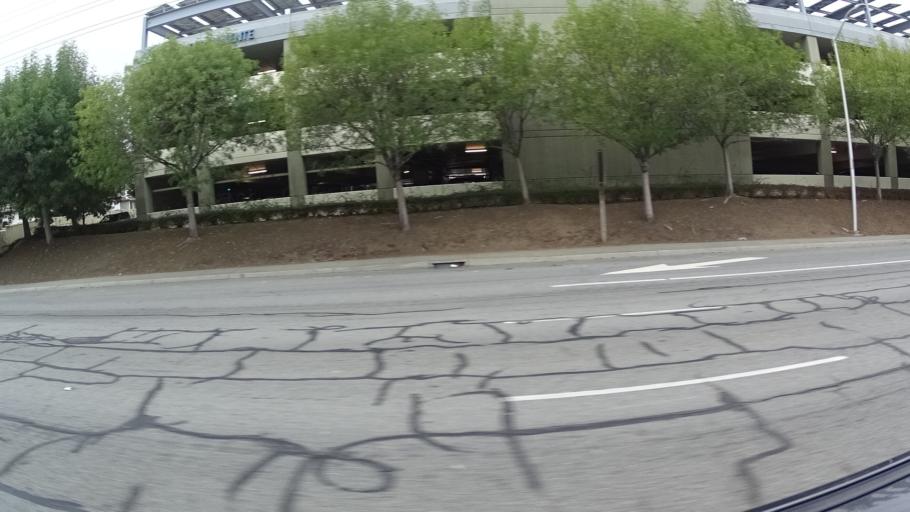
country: US
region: California
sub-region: Santa Clara County
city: Cupertino
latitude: 37.3347
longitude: -121.9957
